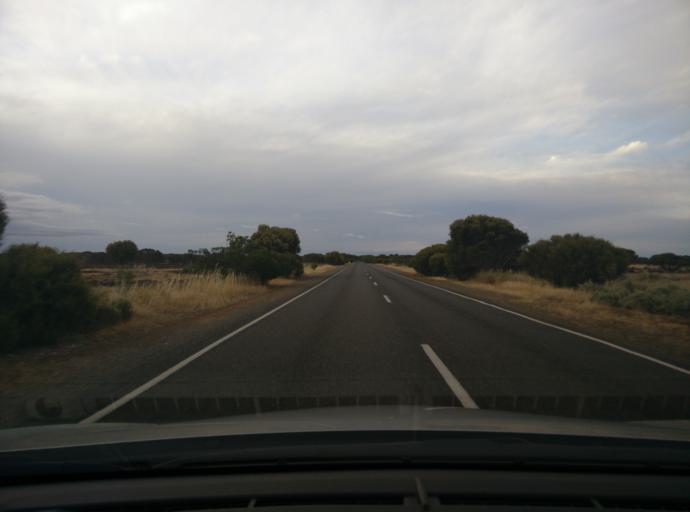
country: AU
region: South Australia
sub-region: Kangaroo Island
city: Kingscote
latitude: -35.7395
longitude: 137.5785
